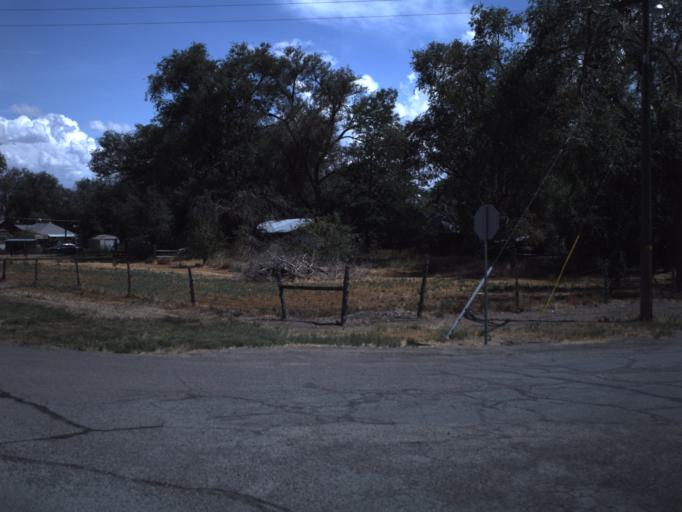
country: US
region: Utah
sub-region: Millard County
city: Delta
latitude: 39.3307
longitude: -112.6694
